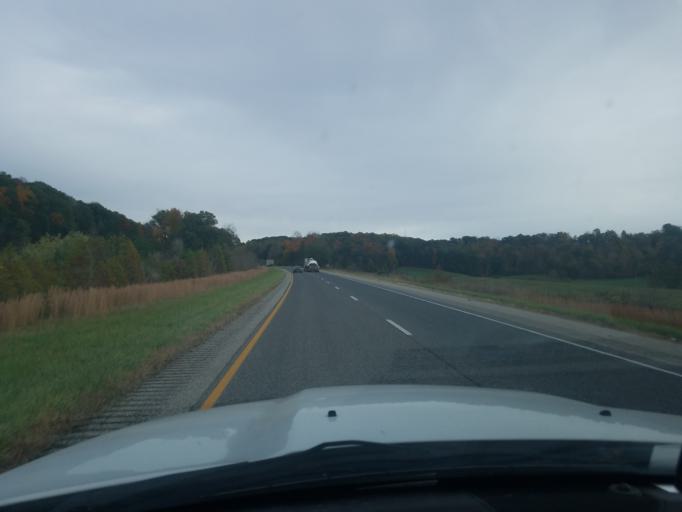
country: US
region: Indiana
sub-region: Dubois County
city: Ferdinand
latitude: 38.2117
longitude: -86.7555
